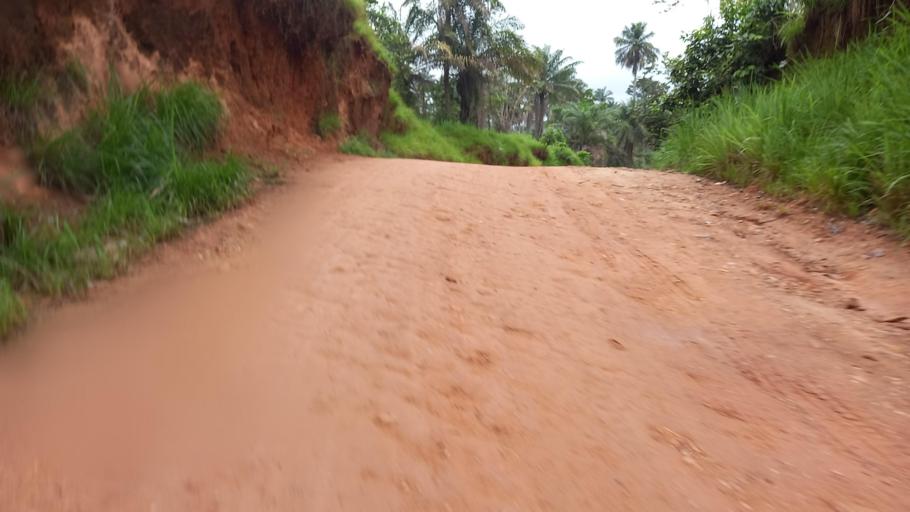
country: SL
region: Eastern Province
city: Kailahun
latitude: 8.2557
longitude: -10.5316
